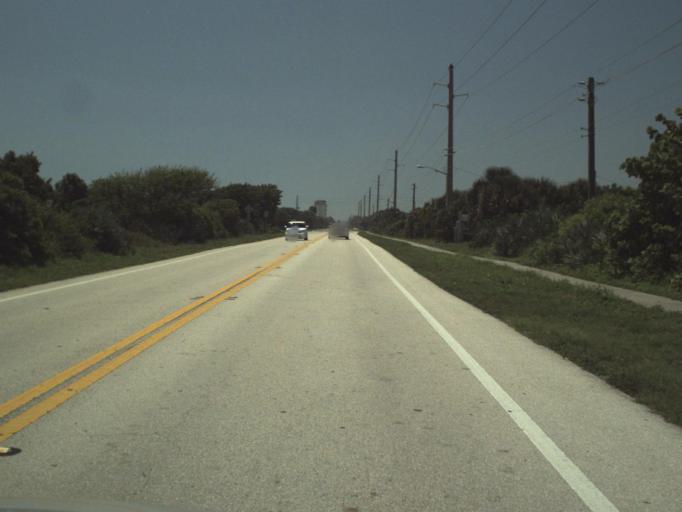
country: US
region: Florida
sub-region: Brevard County
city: Melbourne Beach
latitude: 28.0522
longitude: -80.5501
